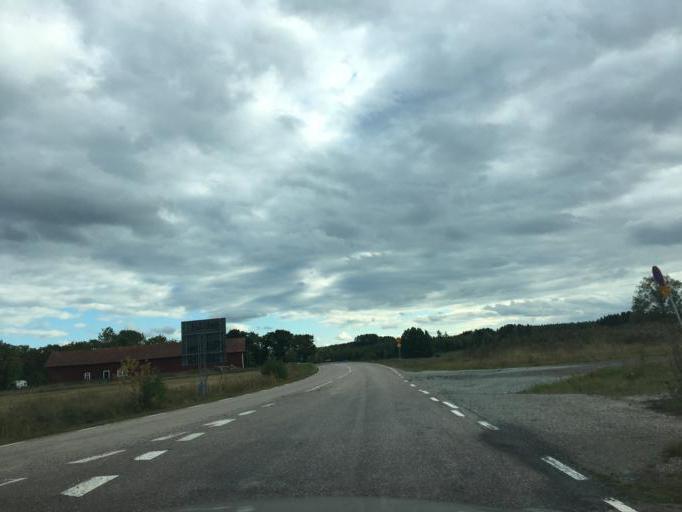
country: SE
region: Uppsala
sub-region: Enkopings Kommun
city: Hummelsta
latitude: 59.6223
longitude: 16.8609
